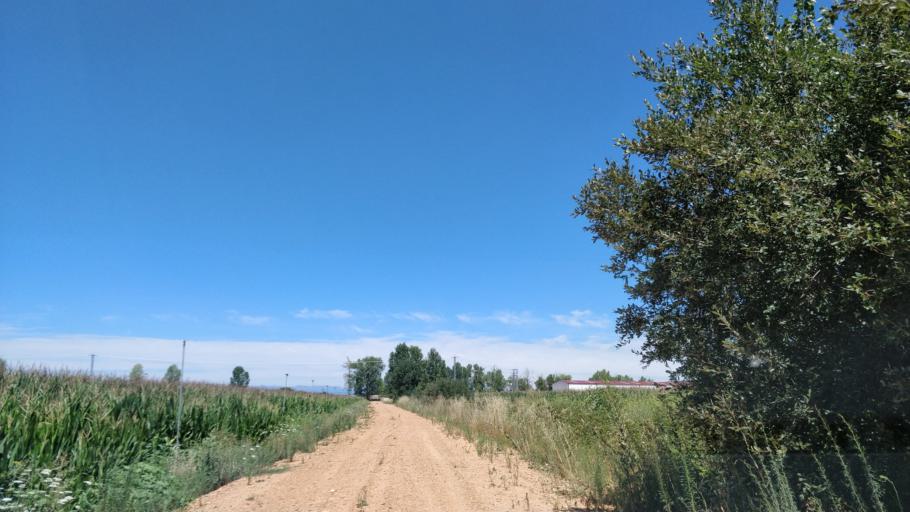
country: ES
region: Castille and Leon
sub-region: Provincia de Leon
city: Bustillo del Paramo
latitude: 42.4762
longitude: -5.8103
